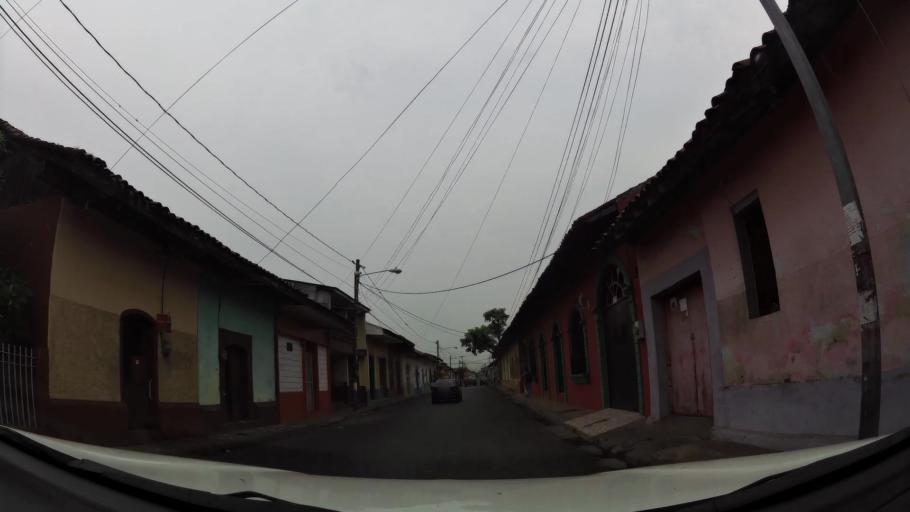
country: NI
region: Leon
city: Leon
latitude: 12.4361
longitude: -86.8855
